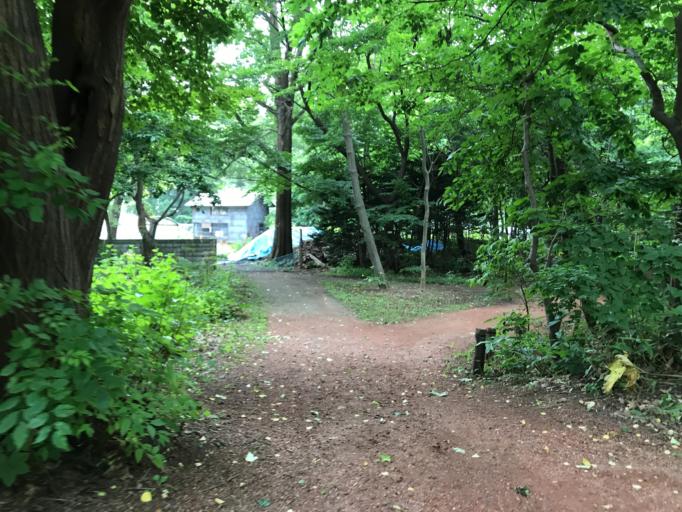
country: JP
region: Hokkaido
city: Sapporo
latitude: 43.0632
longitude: 141.3423
